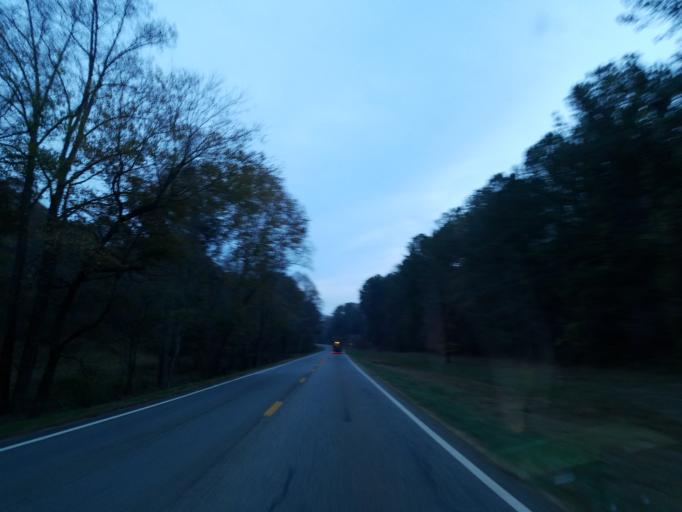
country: US
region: Georgia
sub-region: Pickens County
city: Jasper
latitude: 34.5170
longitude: -84.5677
